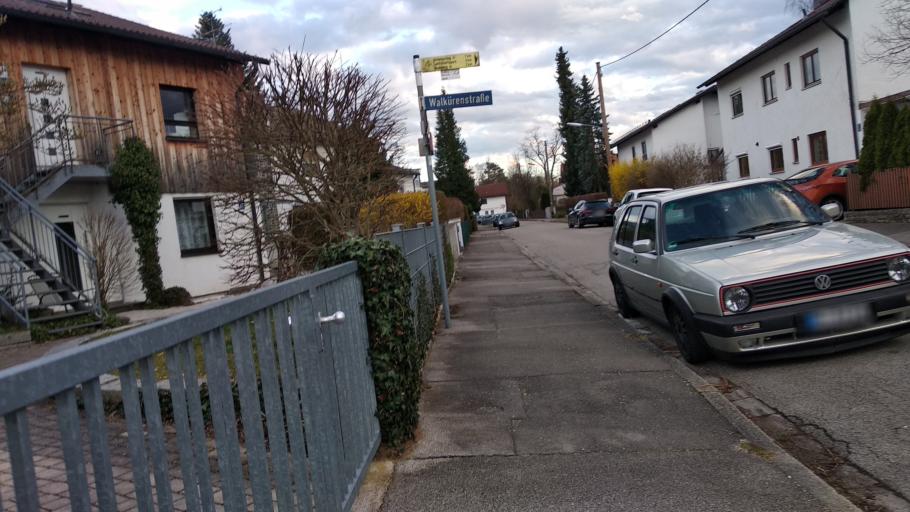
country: DE
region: Bavaria
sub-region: Upper Bavaria
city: Ottobrunn
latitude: 48.0762
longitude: 11.6845
